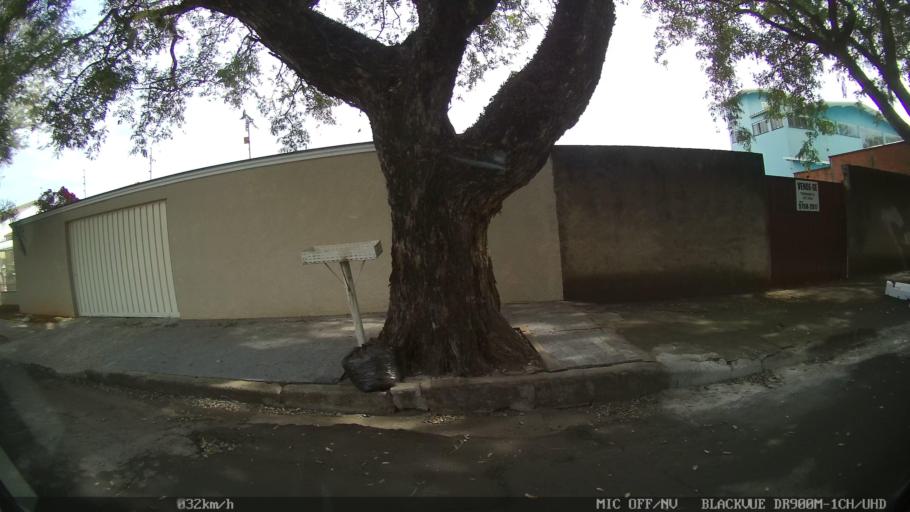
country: BR
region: Sao Paulo
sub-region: Piracicaba
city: Piracicaba
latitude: -22.7181
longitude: -47.6705
